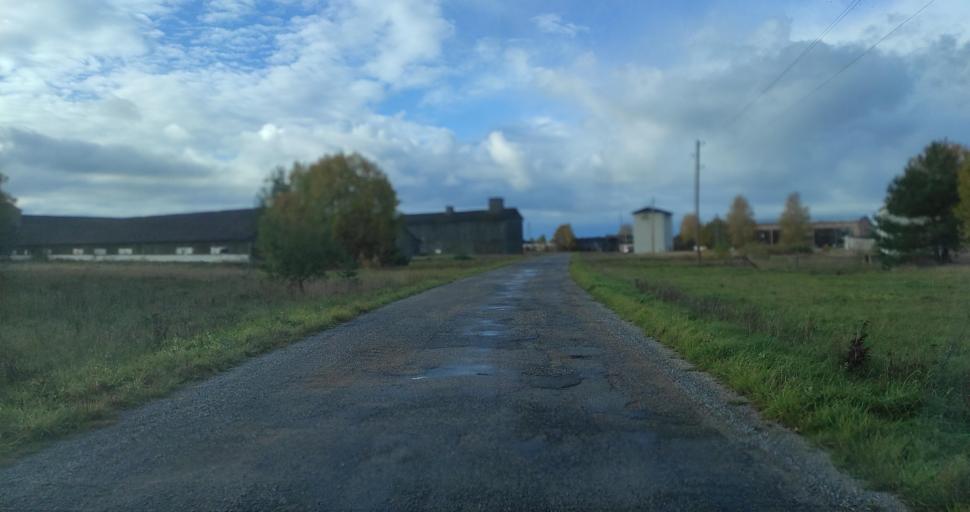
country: LV
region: Skrunda
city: Skrunda
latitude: 56.6867
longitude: 22.0503
